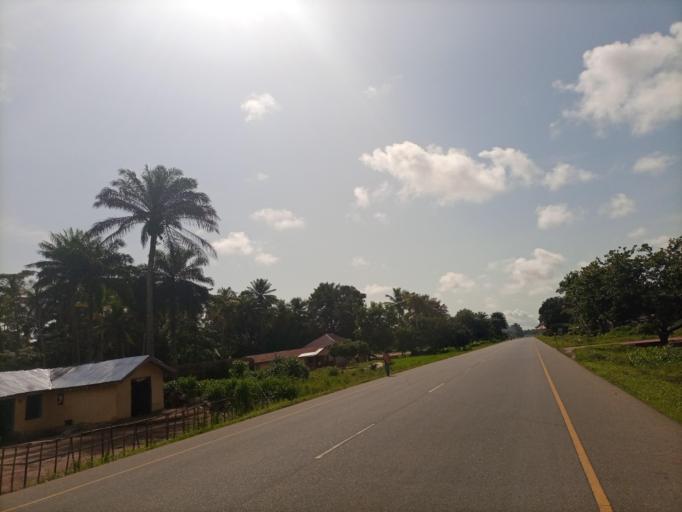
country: SL
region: Northern Province
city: Masoyila
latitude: 8.6260
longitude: -13.1784
